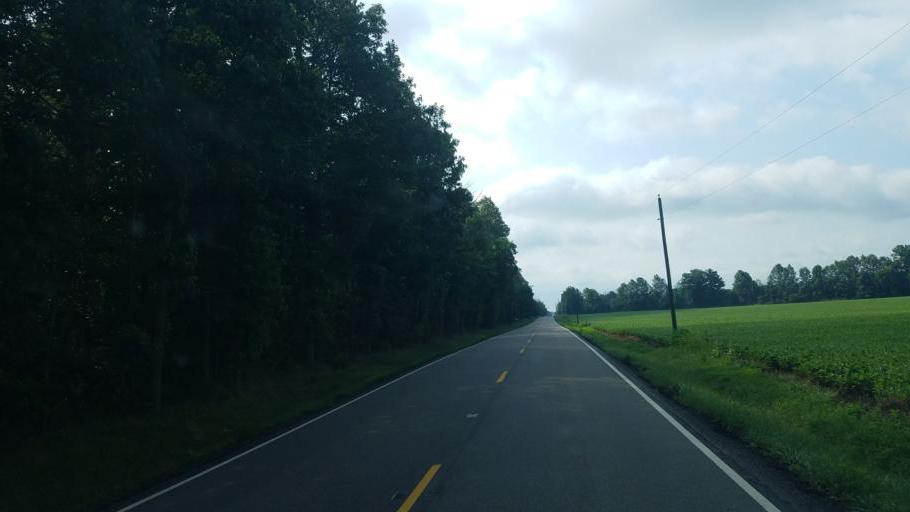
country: US
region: Ohio
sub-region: Knox County
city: Centerburg
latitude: 40.2613
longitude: -82.6000
